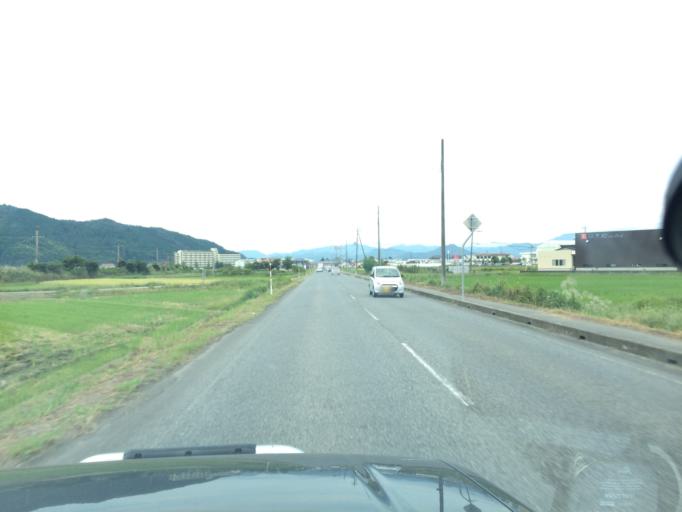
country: JP
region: Hyogo
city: Toyooka
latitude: 35.4894
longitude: 134.7959
